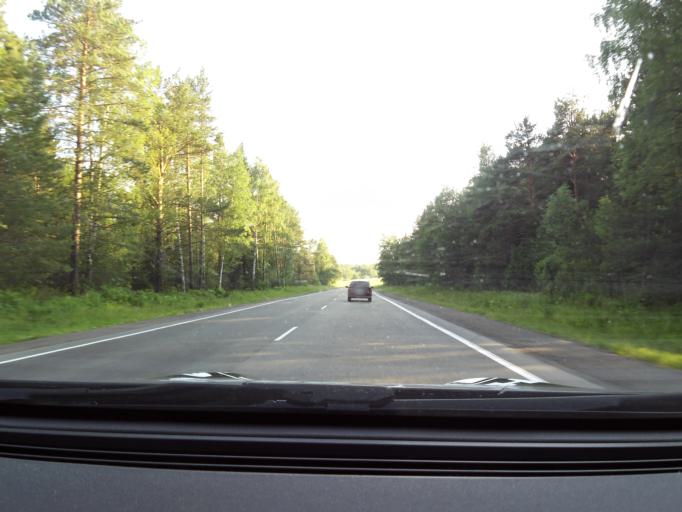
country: RU
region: Sverdlovsk
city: Atig
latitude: 56.7409
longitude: 59.4515
